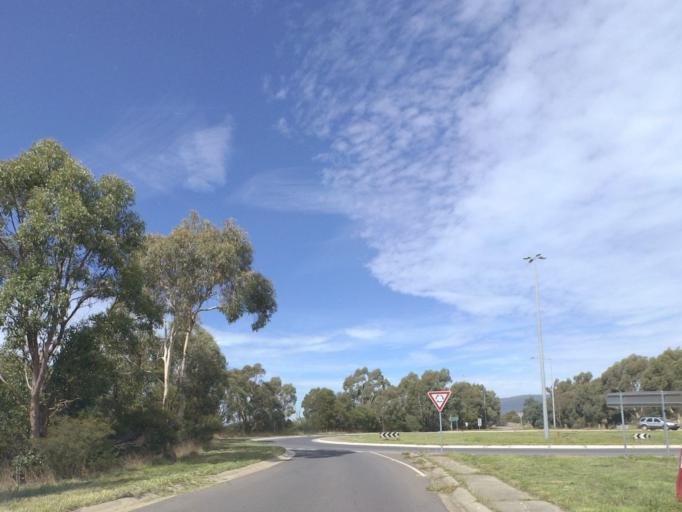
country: AU
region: Victoria
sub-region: Hume
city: Sunbury
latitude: -37.3182
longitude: 144.5275
